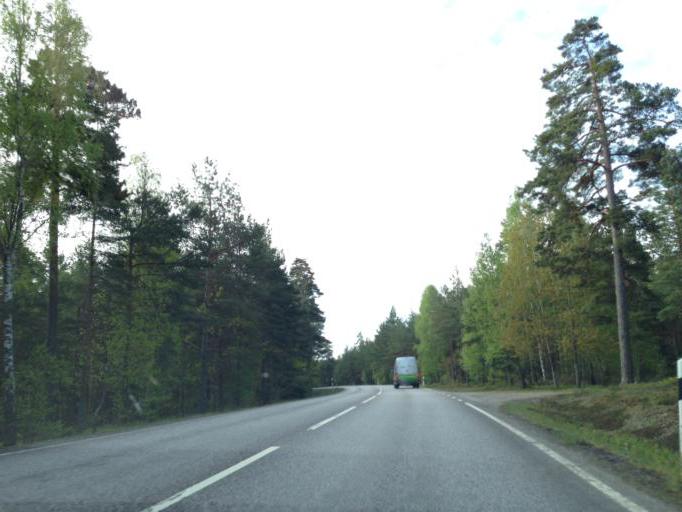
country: SE
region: Soedermanland
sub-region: Nykopings Kommun
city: Stigtomta
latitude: 58.9004
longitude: 16.8246
